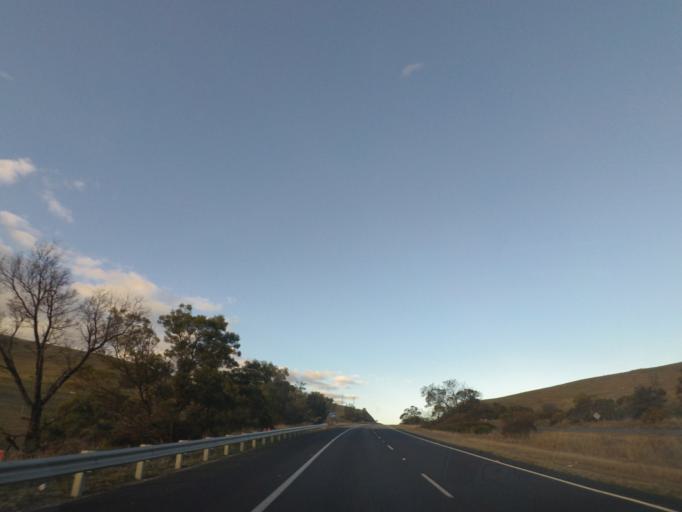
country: AU
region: New South Wales
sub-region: Yass Valley
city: Yass
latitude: -34.7768
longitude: 148.7234
